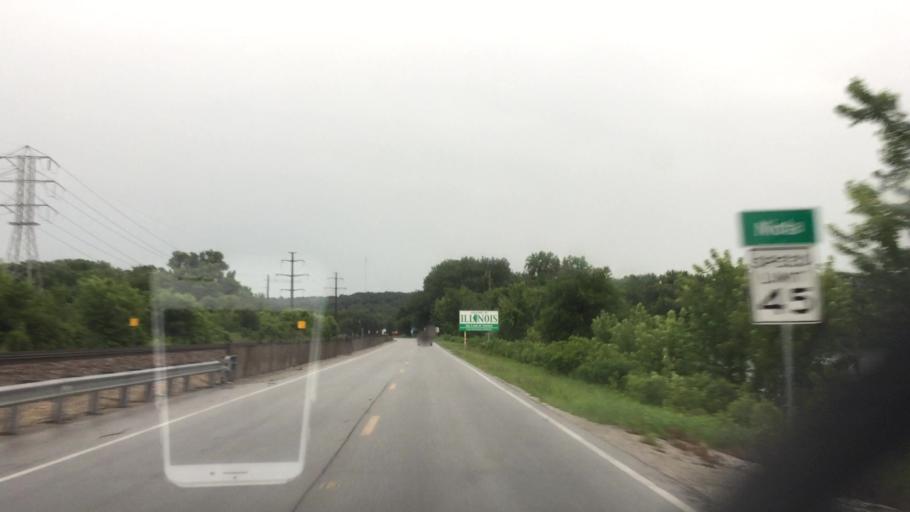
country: US
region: Iowa
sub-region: Lee County
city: Fort Madison
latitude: 40.6217
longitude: -91.2904
